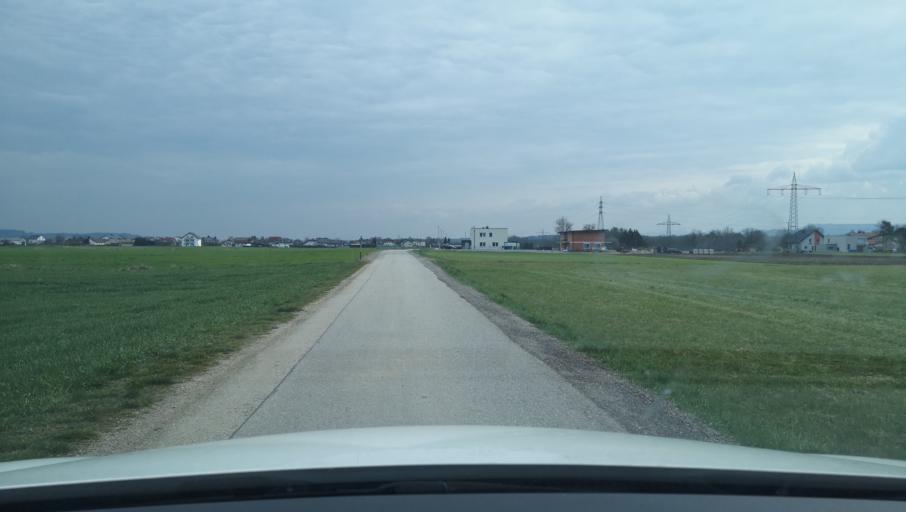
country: AT
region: Lower Austria
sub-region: Politischer Bezirk Amstetten
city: Amstetten
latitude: 48.1129
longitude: 14.9021
